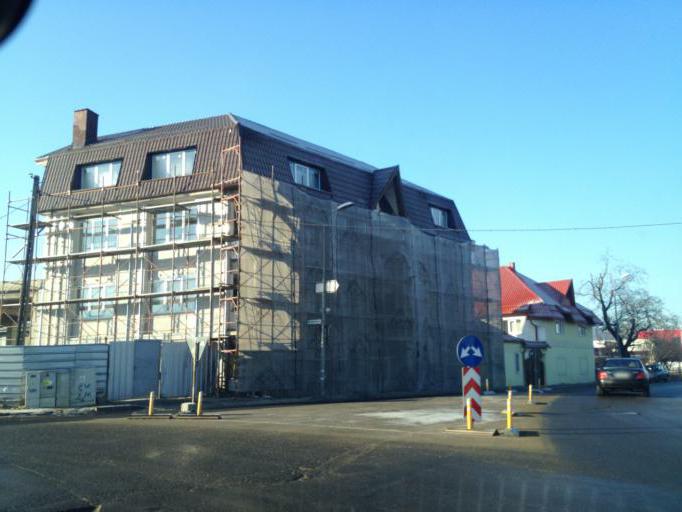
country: RO
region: Brasov
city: Brasov
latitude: 45.6490
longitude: 25.6551
